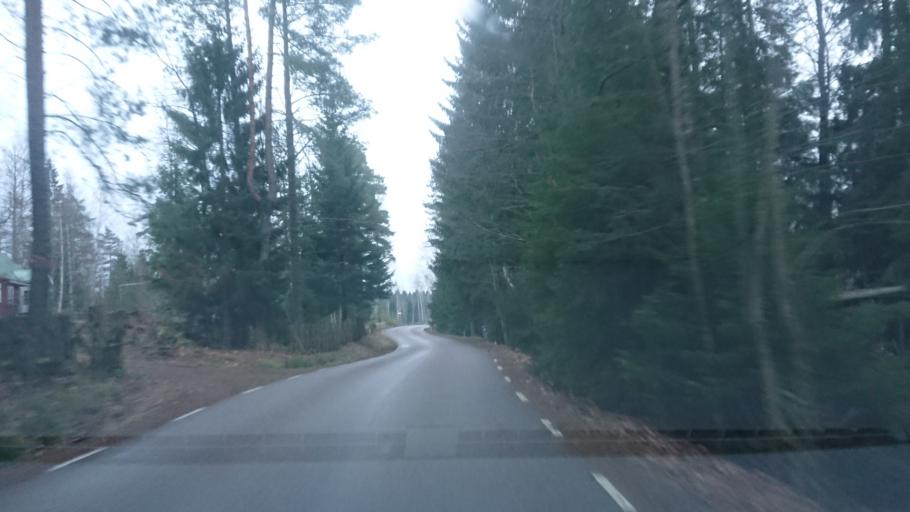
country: SE
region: Uppsala
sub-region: Osthammars Kommun
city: Bjorklinge
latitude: 60.0253
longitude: 17.5737
